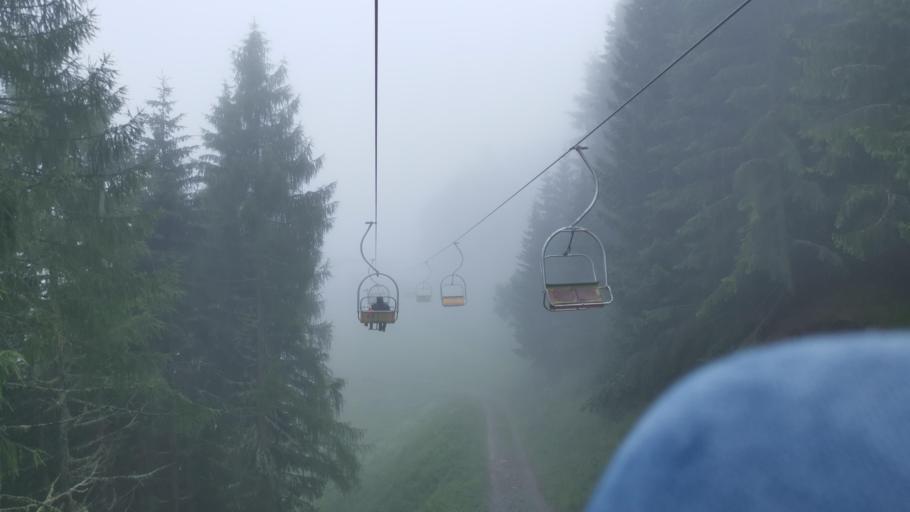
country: AT
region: Tyrol
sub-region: Politischer Bezirk Lienz
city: Leisach
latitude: 46.8187
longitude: 12.7289
